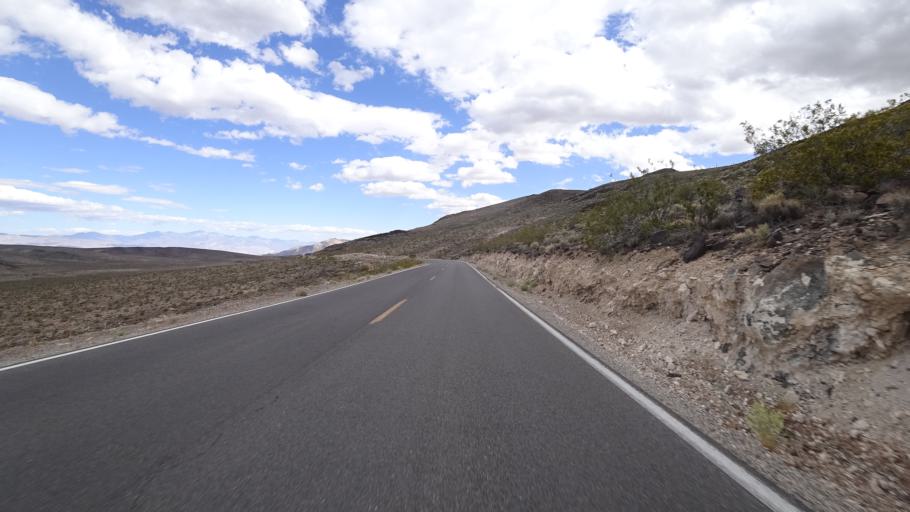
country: US
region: California
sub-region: Inyo County
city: Lone Pine
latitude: 36.3780
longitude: -117.5933
